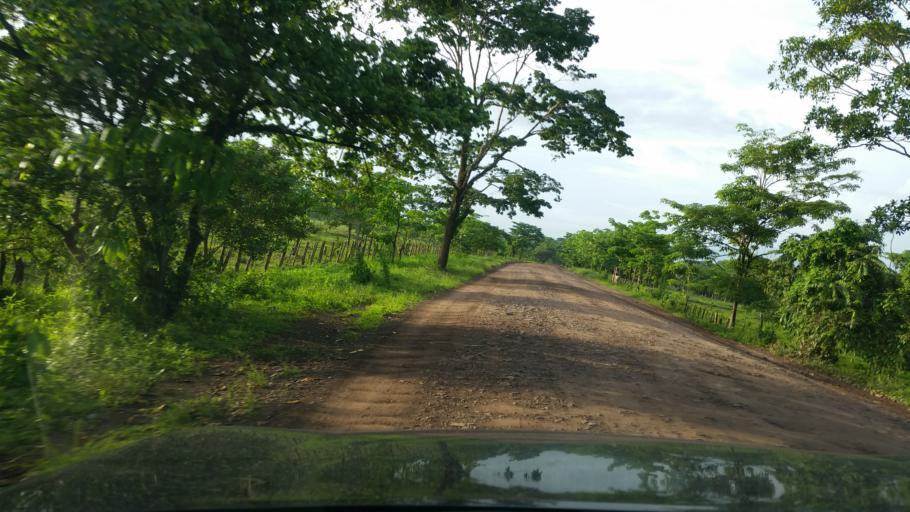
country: NI
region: Atlantico Norte (RAAN)
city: Siuna
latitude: 13.3317
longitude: -84.8905
